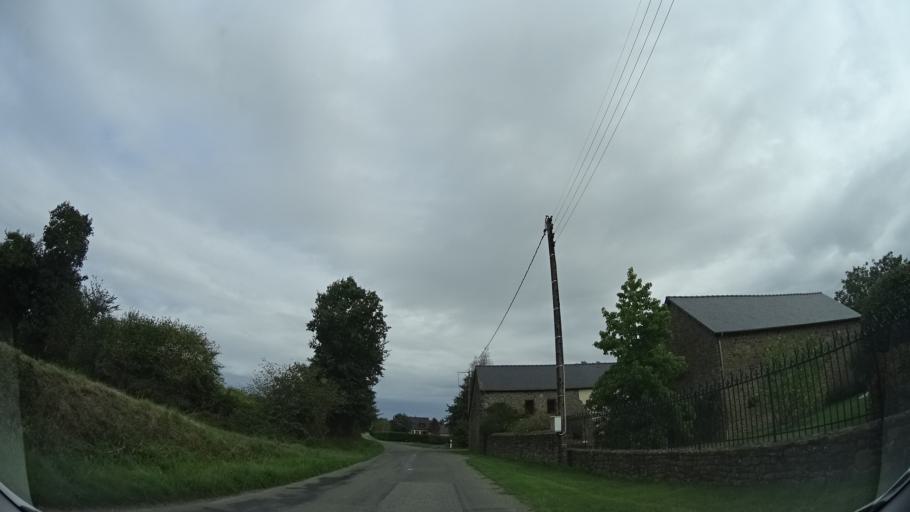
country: FR
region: Brittany
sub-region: Departement d'Ille-et-Vilaine
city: Irodouer
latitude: 48.2899
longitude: -1.9317
